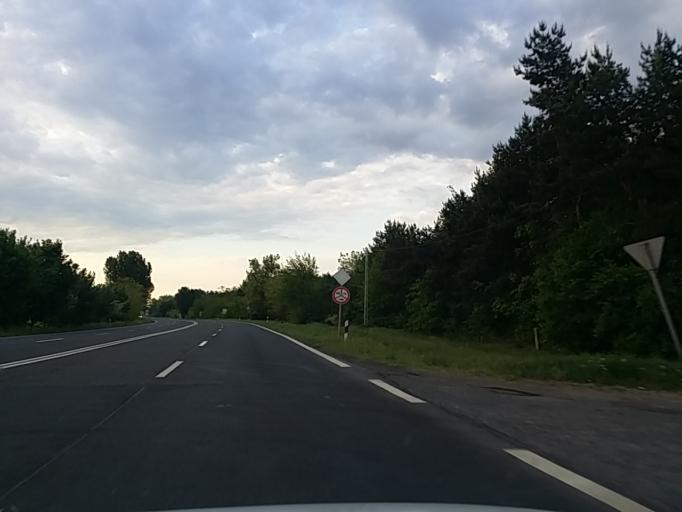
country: HU
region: Bacs-Kiskun
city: Lajosmizse
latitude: 46.9829
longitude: 19.6181
